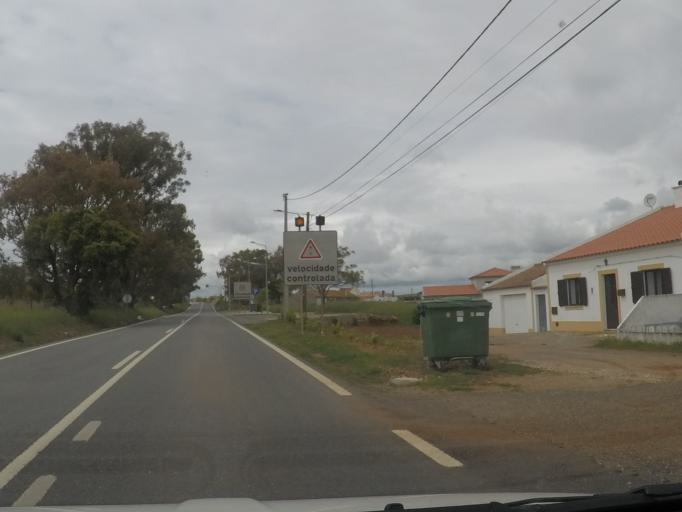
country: PT
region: Setubal
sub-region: Sines
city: Porto Covo
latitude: 37.8633
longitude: -8.7183
